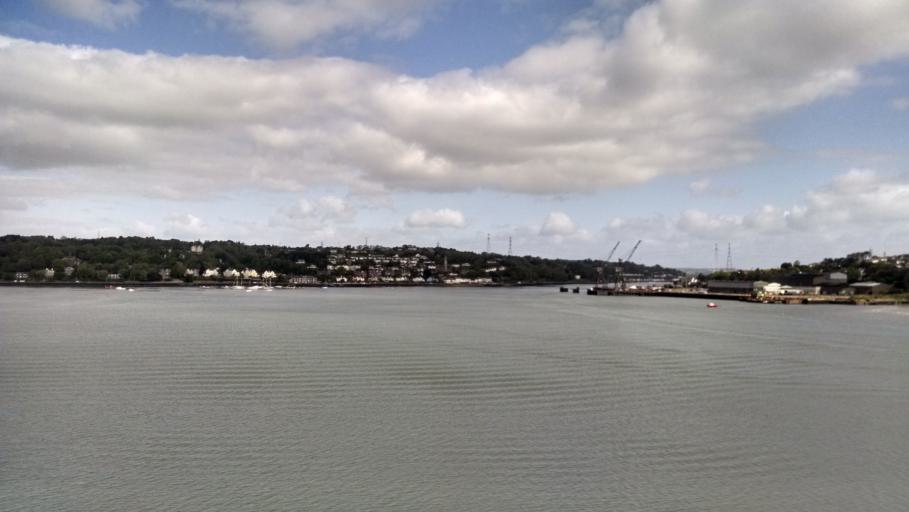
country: IE
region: Munster
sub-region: County Cork
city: Cobh
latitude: 51.8388
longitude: -8.3217
